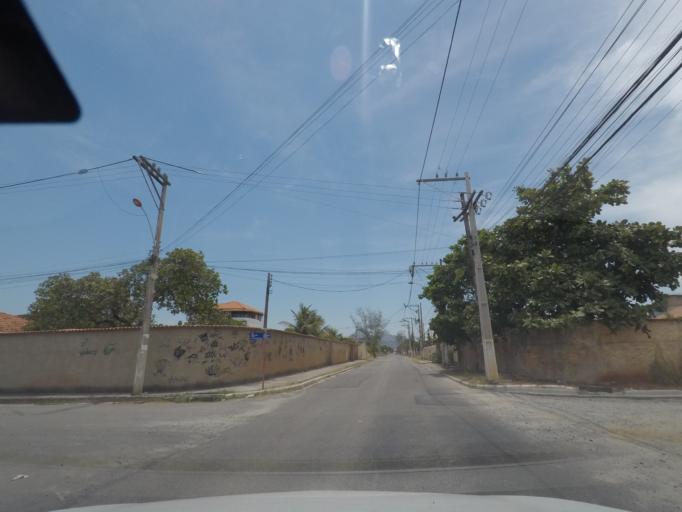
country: BR
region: Rio de Janeiro
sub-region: Marica
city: Marica
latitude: -22.9671
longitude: -42.9539
